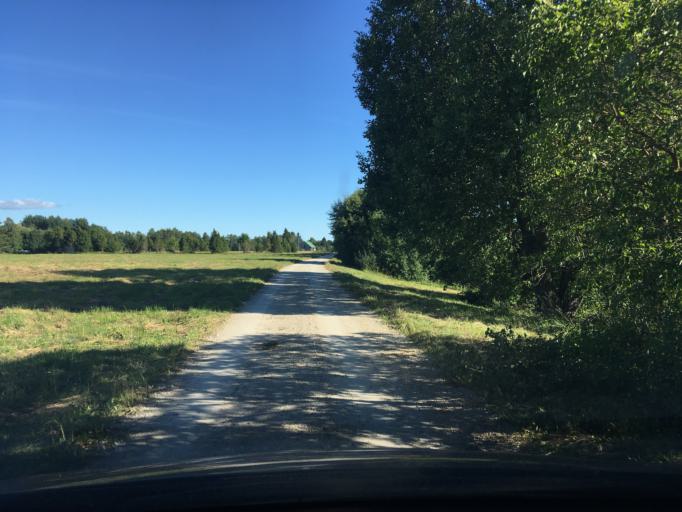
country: EE
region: Laeaene
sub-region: Lihula vald
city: Lihula
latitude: 58.5817
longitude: 23.7370
